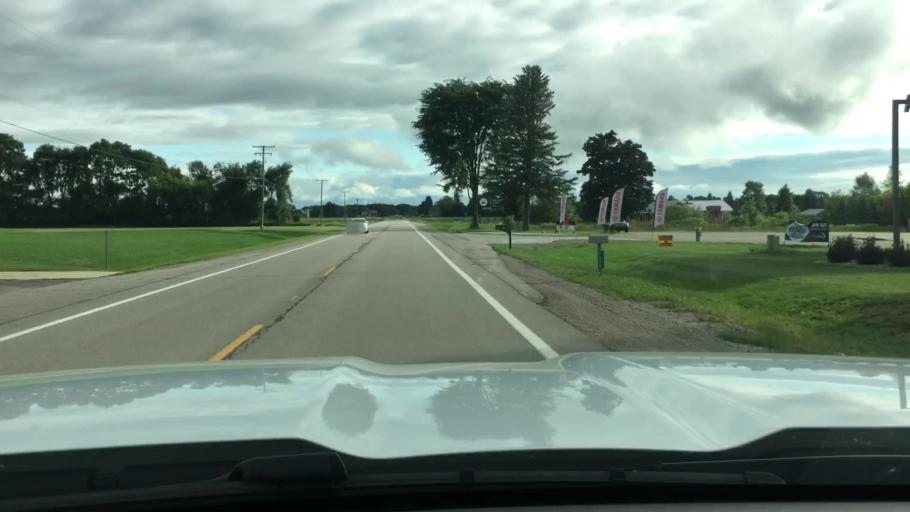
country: US
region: Michigan
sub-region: Tuscola County
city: Caro
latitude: 43.5178
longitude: -83.3583
